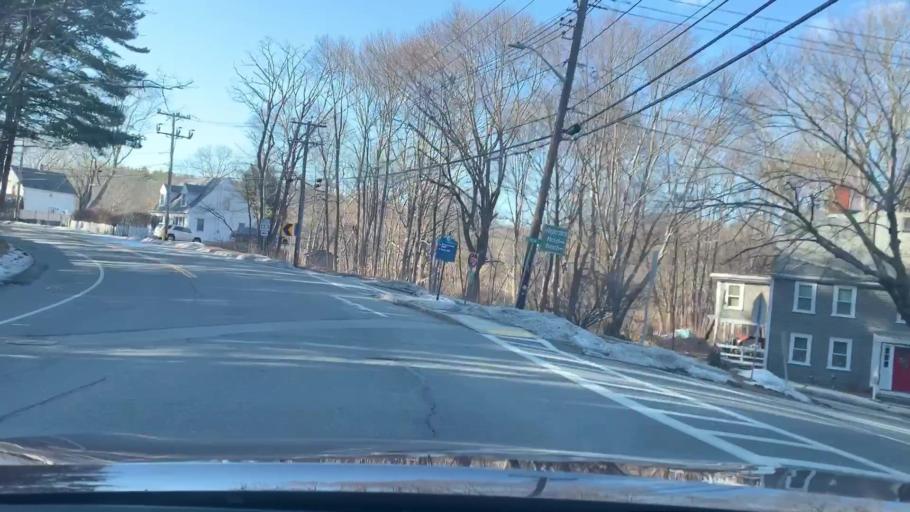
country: US
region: Massachusetts
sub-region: Essex County
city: Gloucester
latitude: 42.6177
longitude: -70.7115
